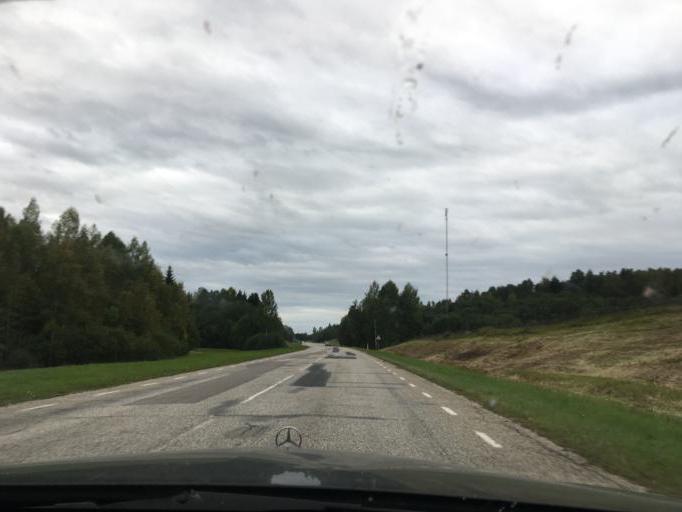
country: LV
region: Aluksnes Rajons
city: Aluksne
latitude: 57.5942
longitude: 27.0908
